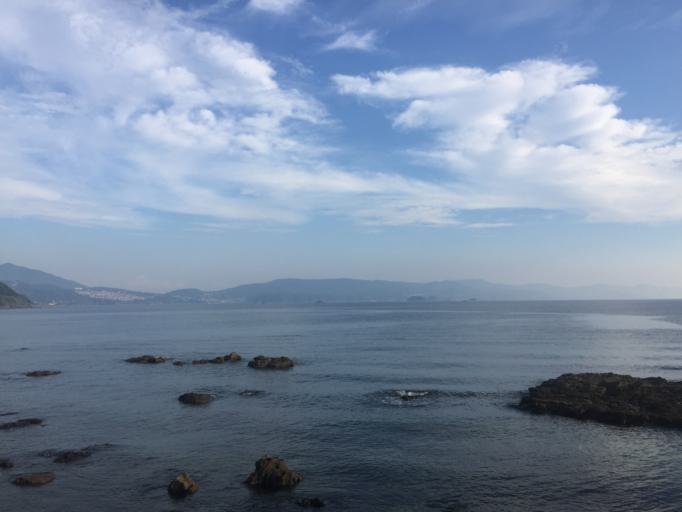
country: JP
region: Nagasaki
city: Nagasaki-shi
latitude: 32.6918
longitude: 129.7844
